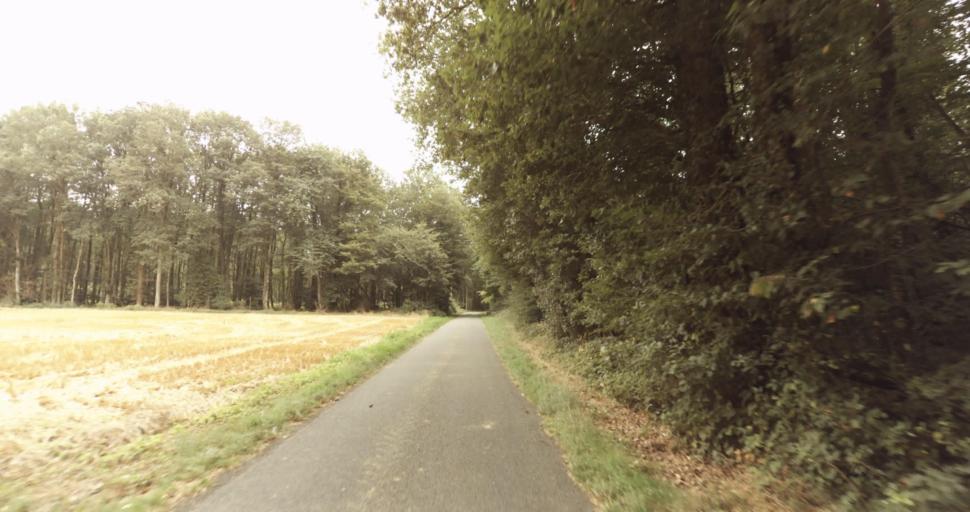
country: FR
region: Centre
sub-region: Departement d'Eure-et-Loir
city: Vert-en-Drouais
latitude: 48.7998
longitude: 1.2877
